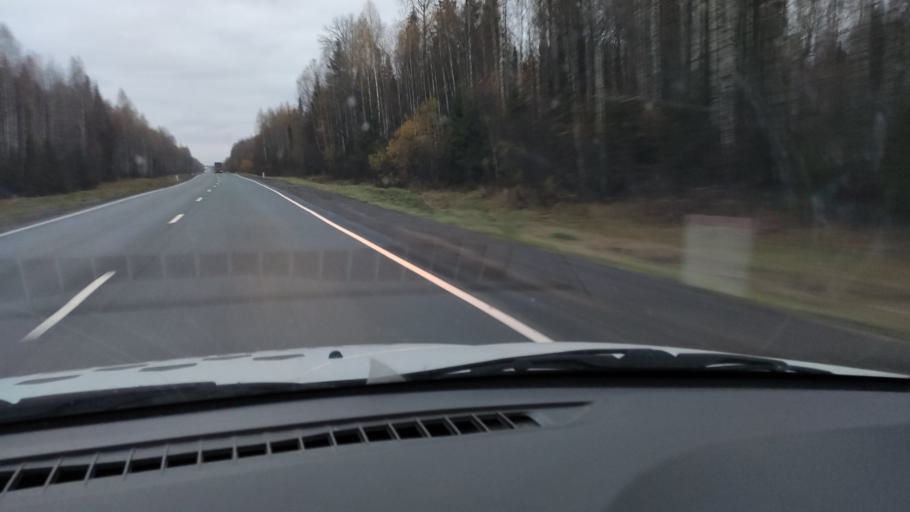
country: RU
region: Kirov
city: Kostino
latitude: 58.8323
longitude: 53.0286
